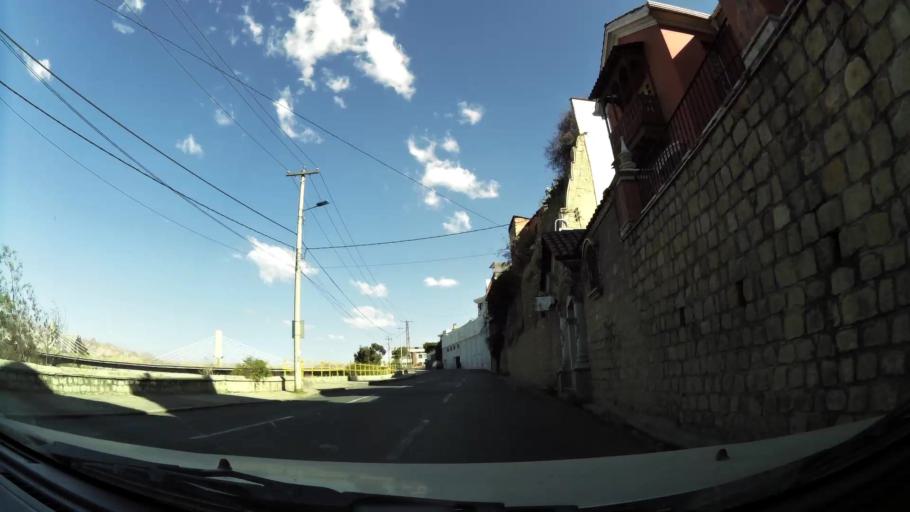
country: BO
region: La Paz
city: La Paz
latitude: -16.5151
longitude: -68.1186
